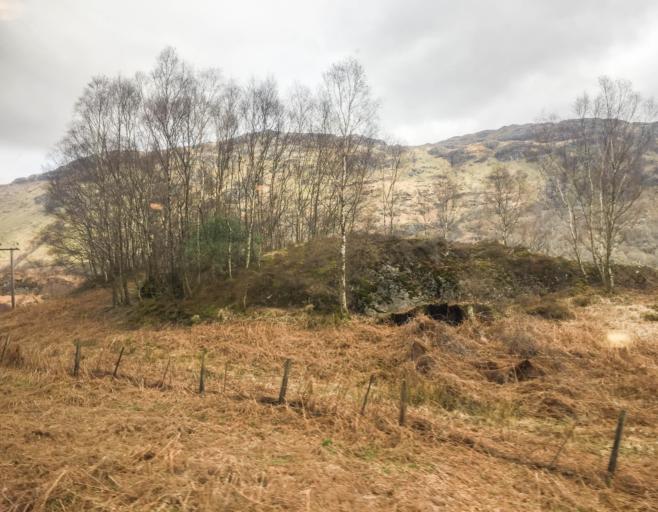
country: GB
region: Scotland
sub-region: Argyll and Bute
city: Garelochhead
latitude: 56.2776
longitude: -4.7079
